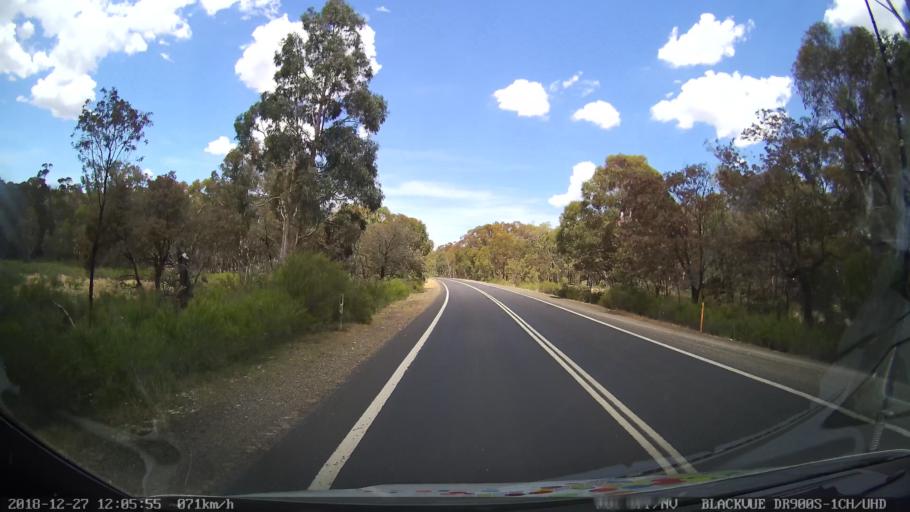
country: AU
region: New South Wales
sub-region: Blayney
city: Blayney
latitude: -33.8045
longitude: 149.3331
